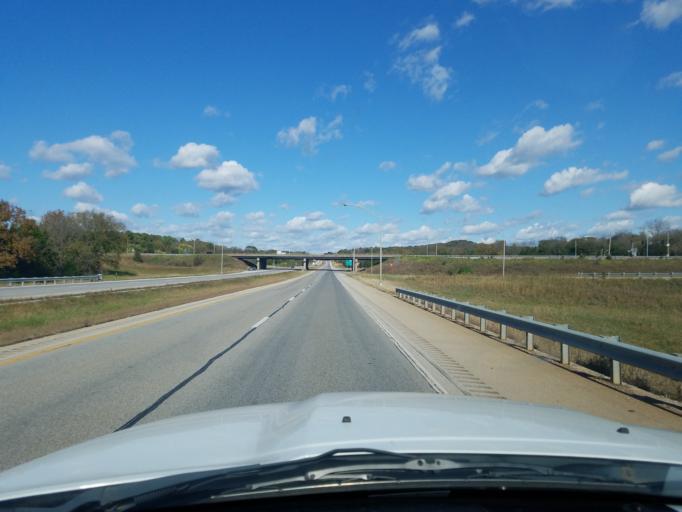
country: US
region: Kentucky
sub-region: Warren County
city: Bowling Green
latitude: 36.9902
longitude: -86.5035
